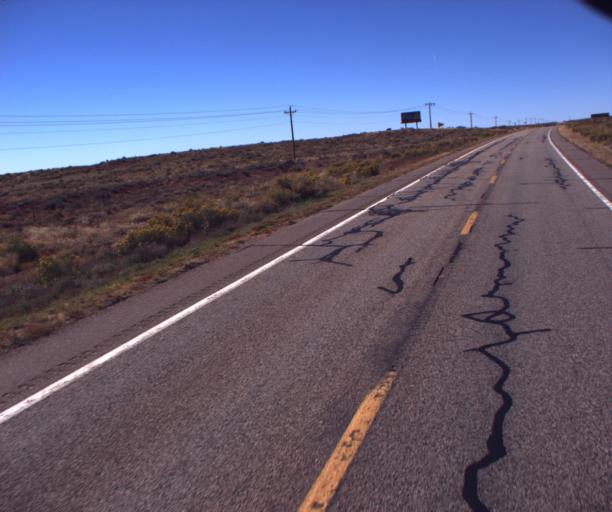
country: US
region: Arizona
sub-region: Coconino County
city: Fredonia
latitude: 36.8799
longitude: -112.6451
